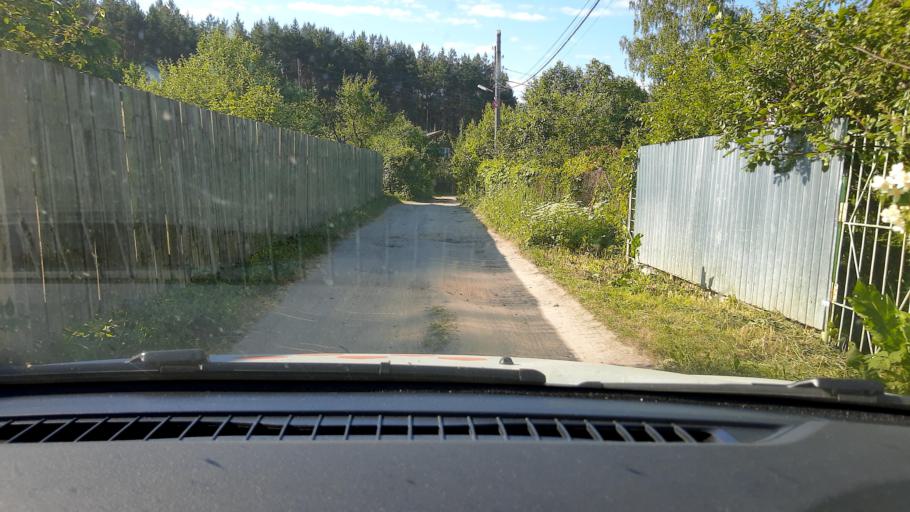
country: RU
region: Nizjnij Novgorod
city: Neklyudovo
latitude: 56.4282
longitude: 44.0097
